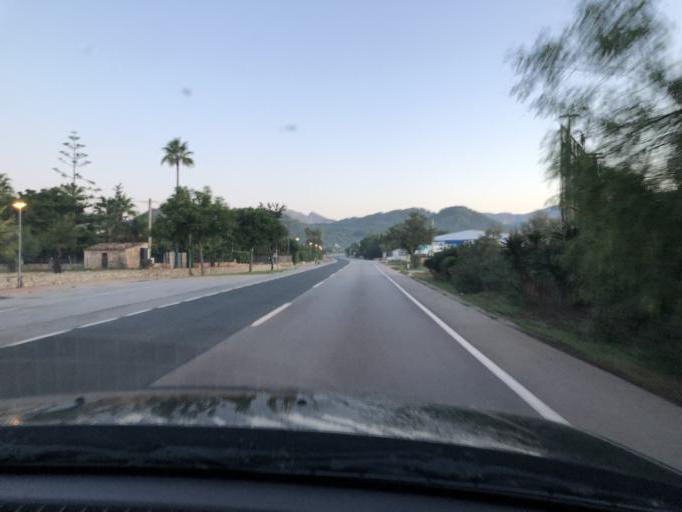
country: ES
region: Balearic Islands
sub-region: Illes Balears
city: Camp de Mar
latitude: 39.5544
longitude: 2.3991
